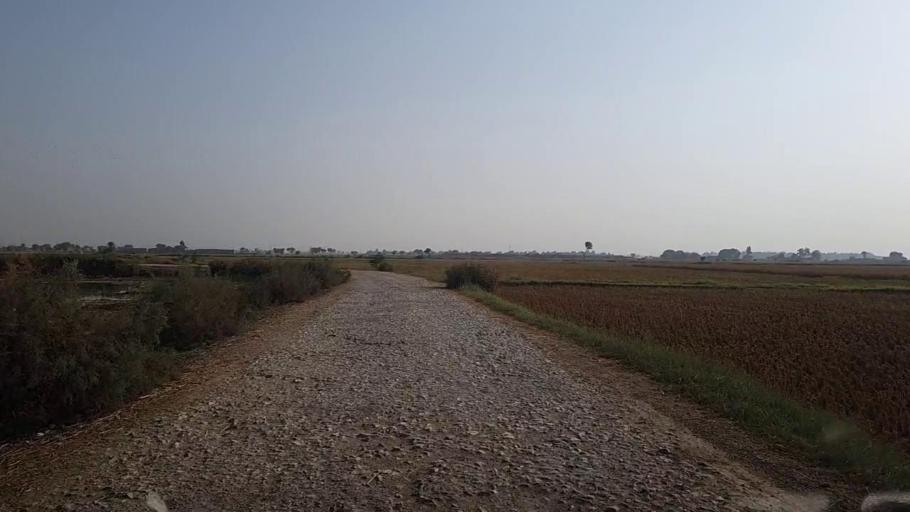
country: PK
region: Sindh
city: Kandhkot
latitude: 28.2905
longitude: 69.2534
